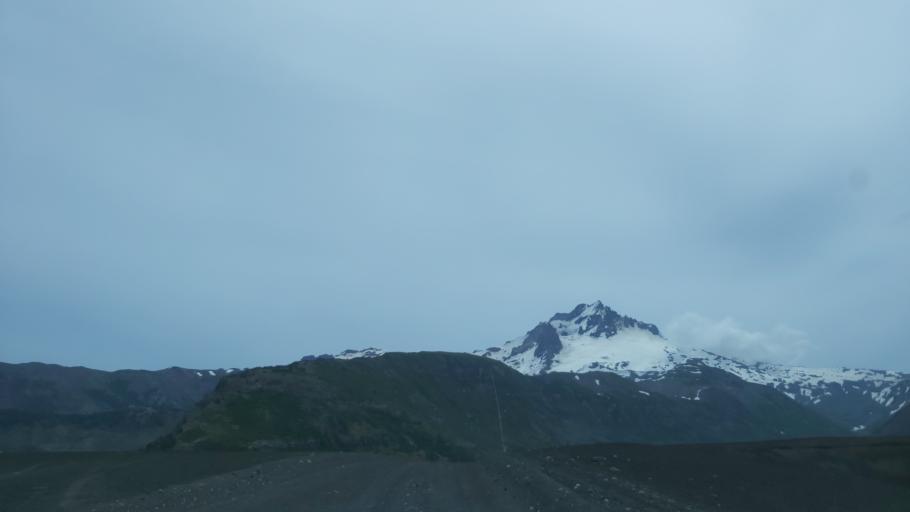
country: AR
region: Neuquen
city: Andacollo
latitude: -37.4612
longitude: -71.3091
